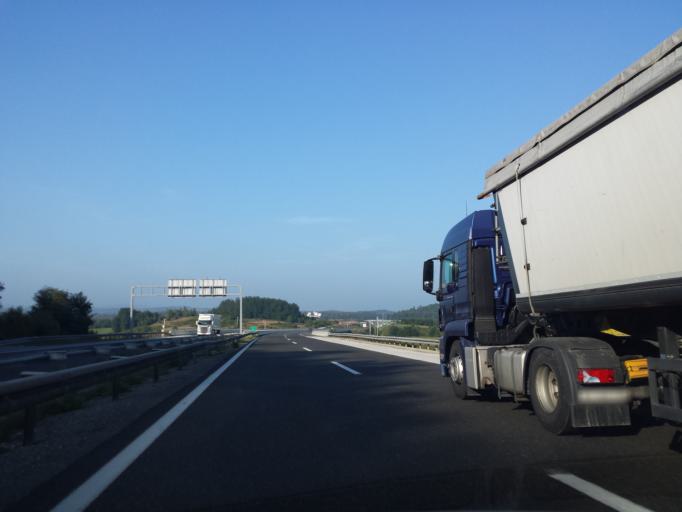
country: HR
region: Karlovacka
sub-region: Grad Ogulin
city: Ogulin
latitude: 45.4125
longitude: 15.2789
